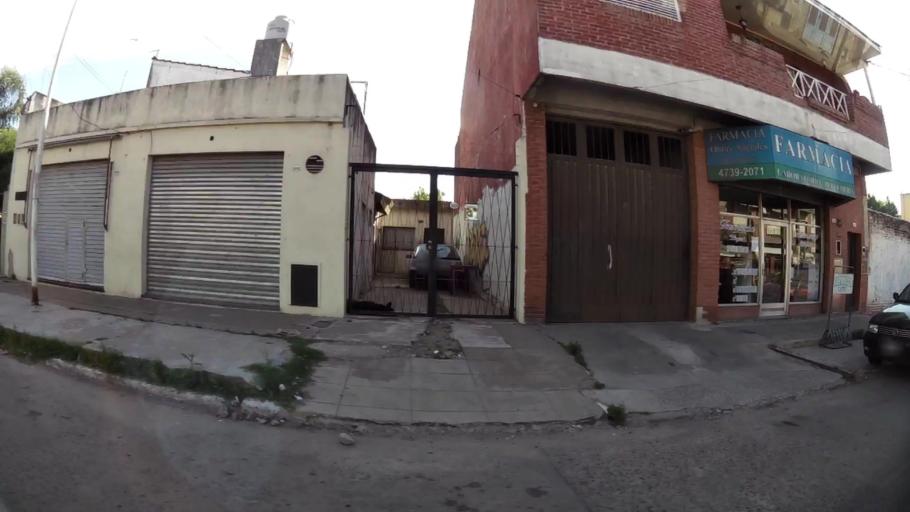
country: AR
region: Buenos Aires
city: Hurlingham
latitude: -34.5729
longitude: -58.6178
